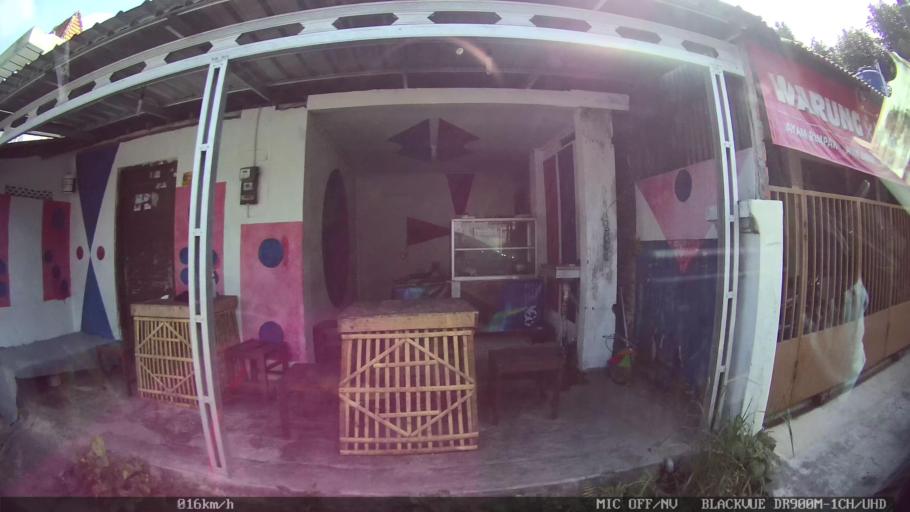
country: ID
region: Daerah Istimewa Yogyakarta
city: Yogyakarta
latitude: -7.8063
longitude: 110.3756
